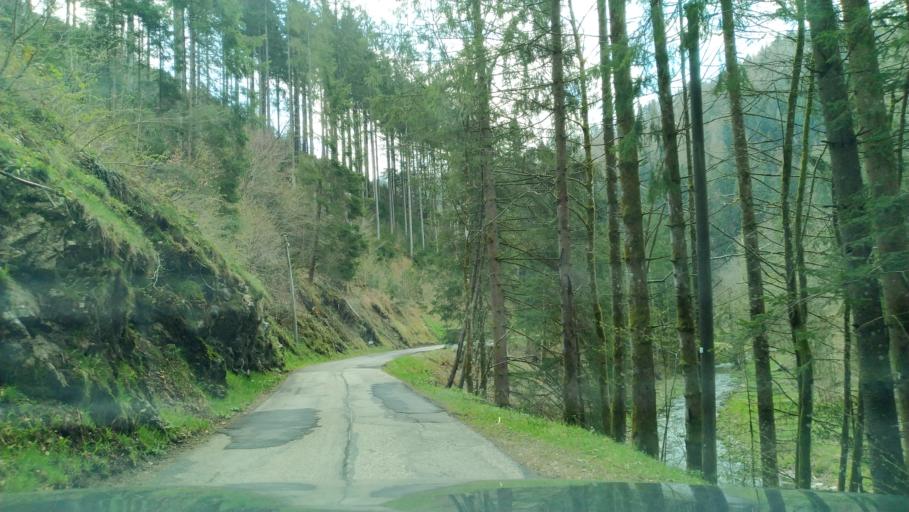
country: DE
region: Baden-Wuerttemberg
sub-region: Freiburg Region
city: Gutenbach
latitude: 48.0151
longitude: 8.1350
